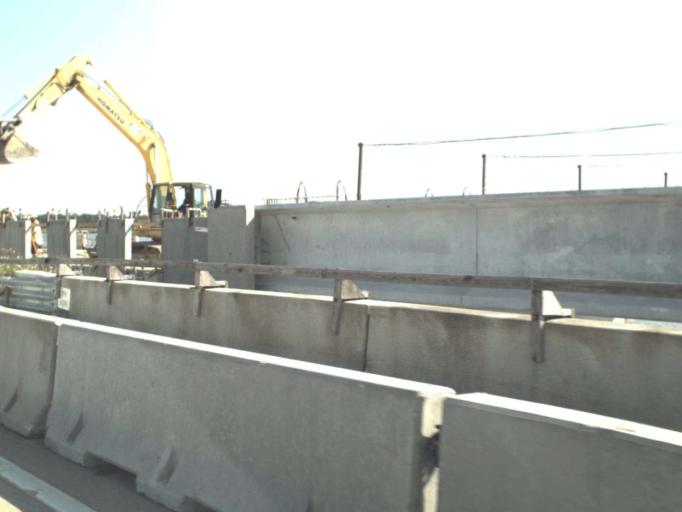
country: US
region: Florida
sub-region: Walton County
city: Freeport
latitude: 30.4251
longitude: -86.1569
